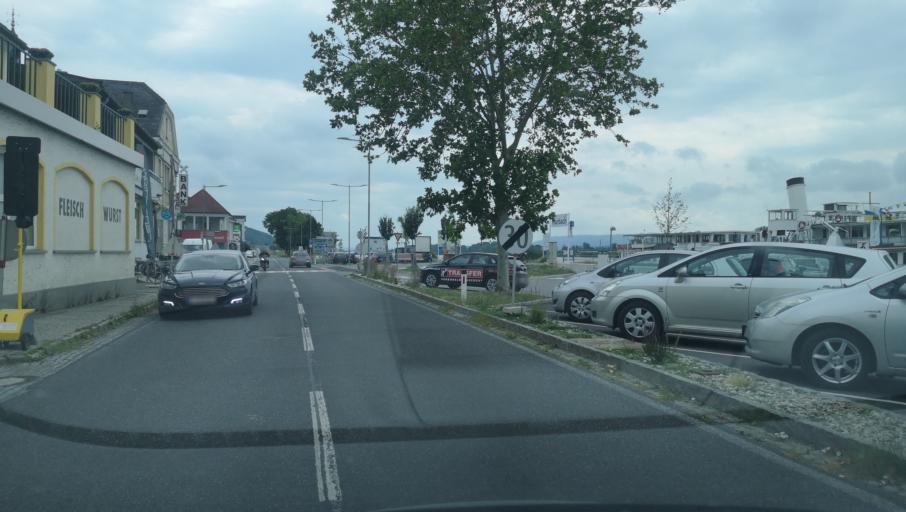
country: AT
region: Lower Austria
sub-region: Politischer Bezirk Melk
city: Marbach an der Donau
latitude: 48.2141
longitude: 15.1512
